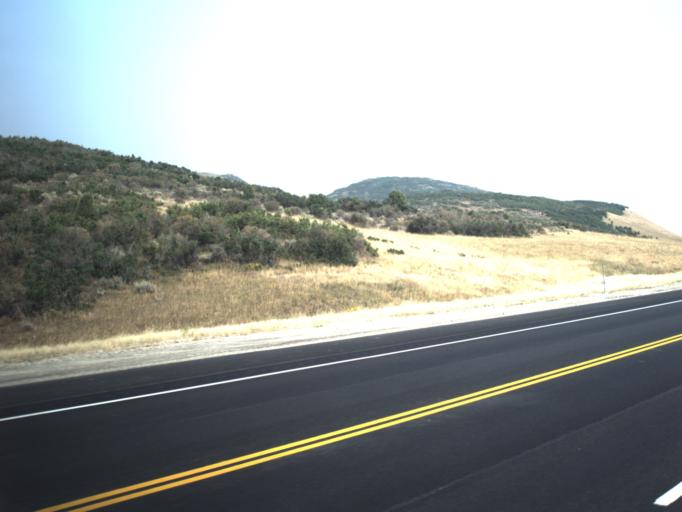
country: US
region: Utah
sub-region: Summit County
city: Park City
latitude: 40.6338
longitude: -111.3900
